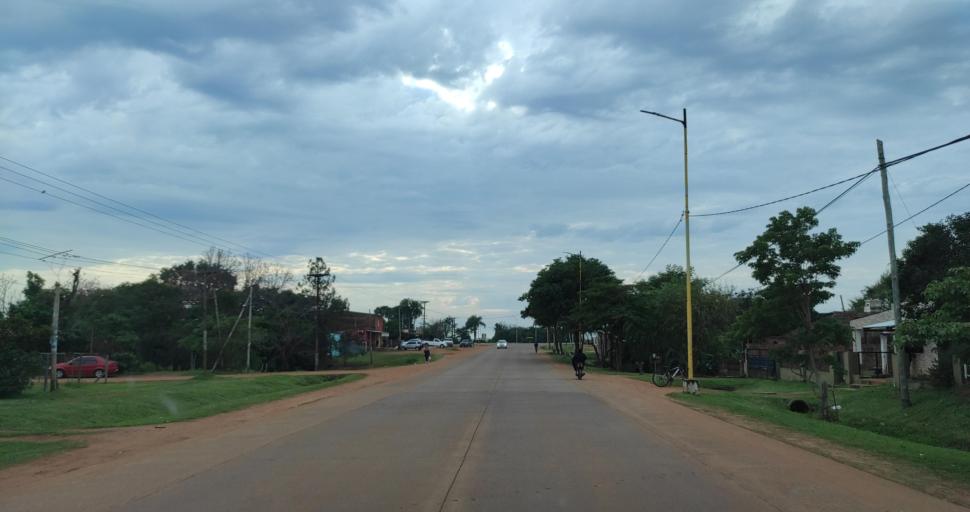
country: AR
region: Corrientes
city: Santo Tome
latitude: -28.5480
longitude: -56.0633
